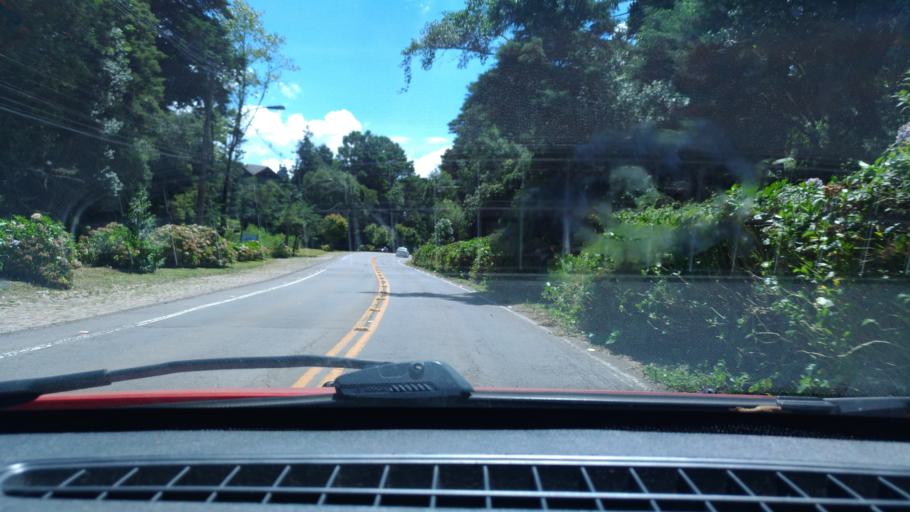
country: BR
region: Rio Grande do Sul
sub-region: Canela
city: Canela
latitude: -29.3566
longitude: -50.8287
